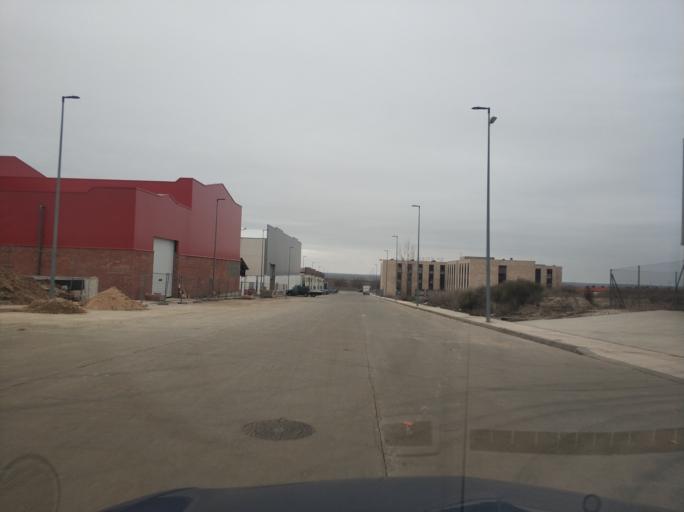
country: ES
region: Castille and Leon
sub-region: Provincia de Salamanca
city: Castellanos de Moriscos
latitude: 41.0094
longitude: -5.6063
